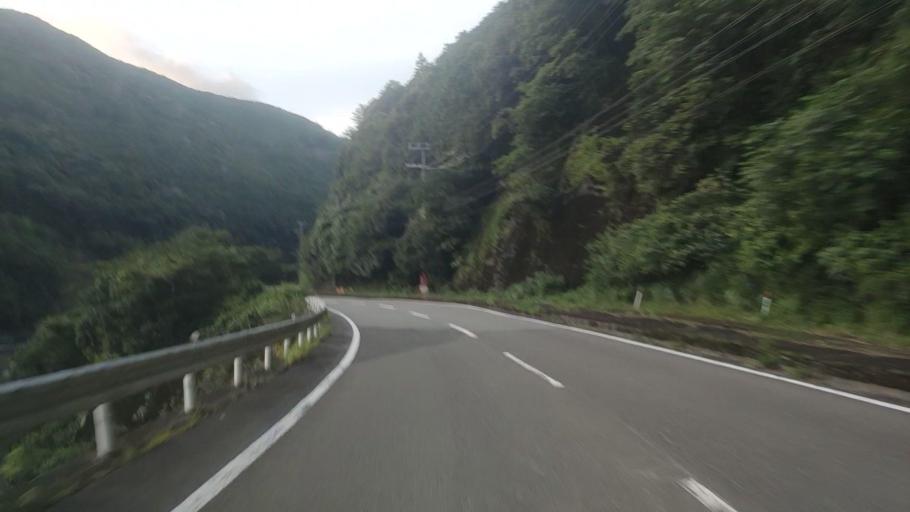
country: JP
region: Wakayama
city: Shingu
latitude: 33.8184
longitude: 135.7676
